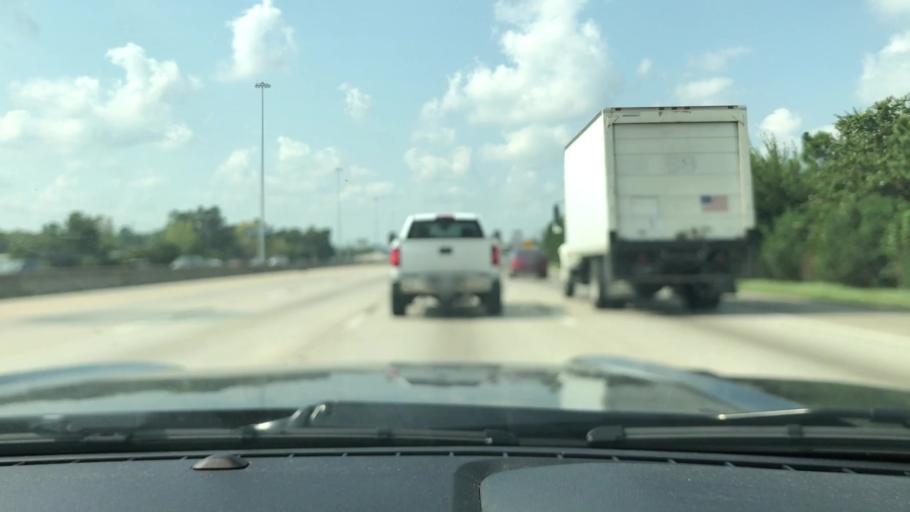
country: US
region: Texas
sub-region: Harris County
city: Aldine
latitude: 29.8972
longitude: -95.3146
